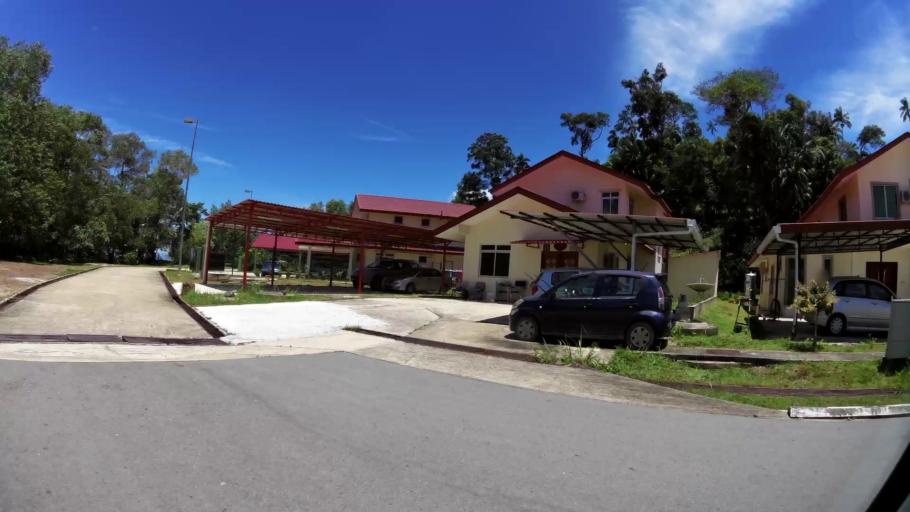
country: BN
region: Brunei and Muara
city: Bandar Seri Begawan
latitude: 5.0145
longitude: 115.0306
